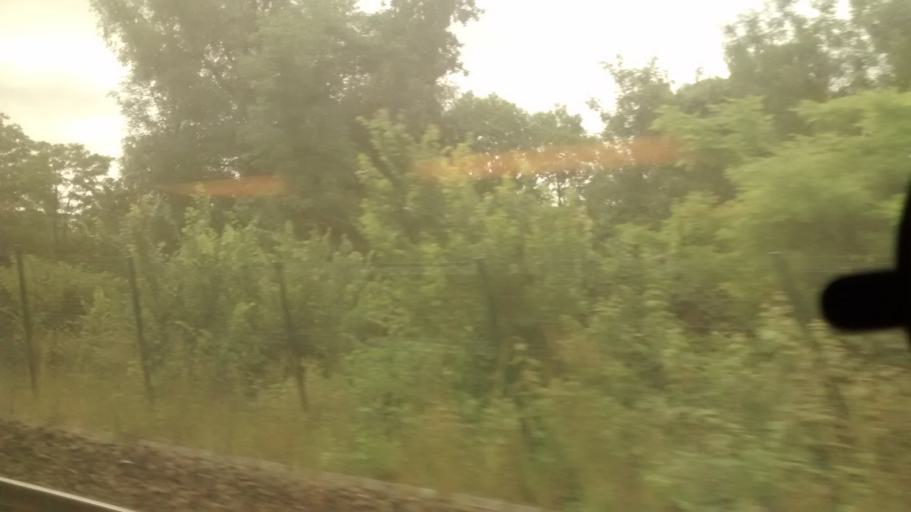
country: FR
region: Ile-de-France
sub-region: Departement de l'Essonne
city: Wissous
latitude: 48.7403
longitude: 2.3341
